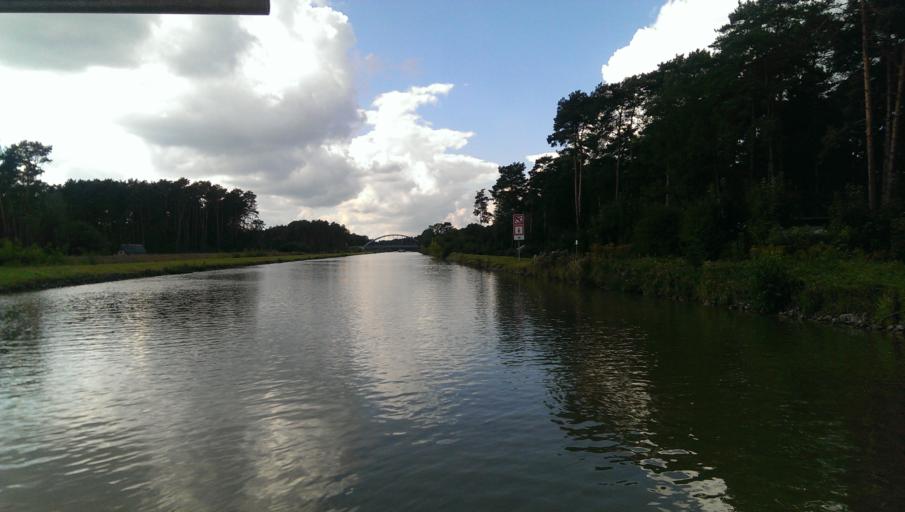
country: DE
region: Brandenburg
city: Marienwerder
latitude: 52.8560
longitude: 13.6628
